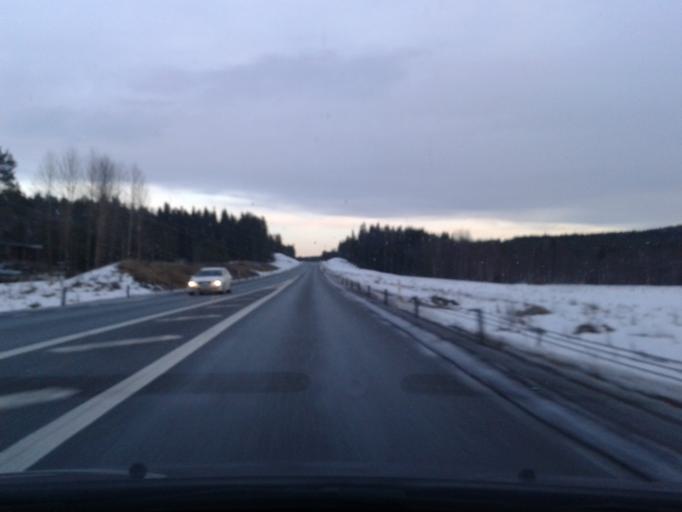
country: SE
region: Vaesternorrland
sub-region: Kramfors Kommun
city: Bollstabruk
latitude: 63.0744
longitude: 17.5586
